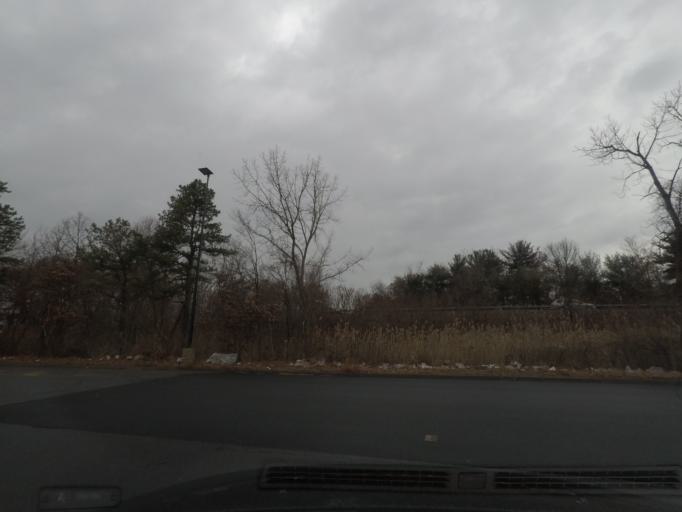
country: US
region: New York
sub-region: Albany County
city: Colonie
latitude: 42.7075
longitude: -73.8264
